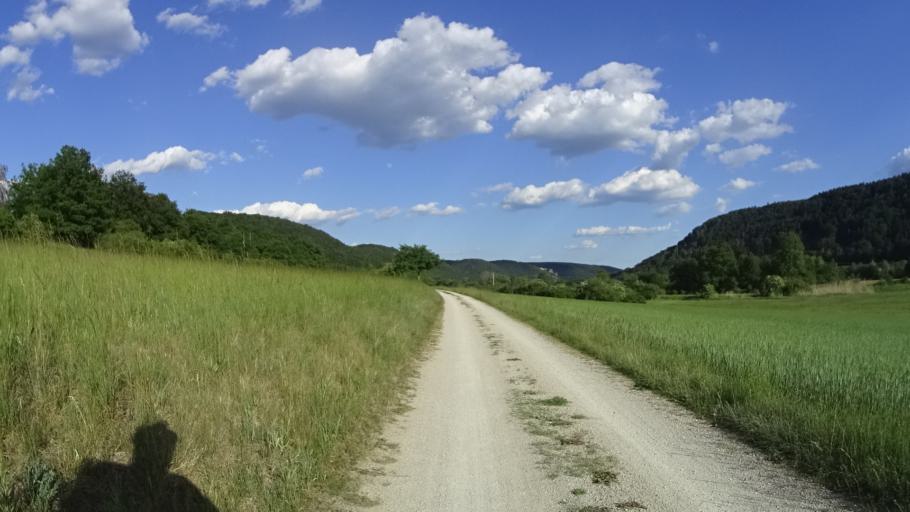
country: DE
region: Bavaria
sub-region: Upper Palatinate
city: Dietfurt
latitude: 49.0169
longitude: 11.6057
